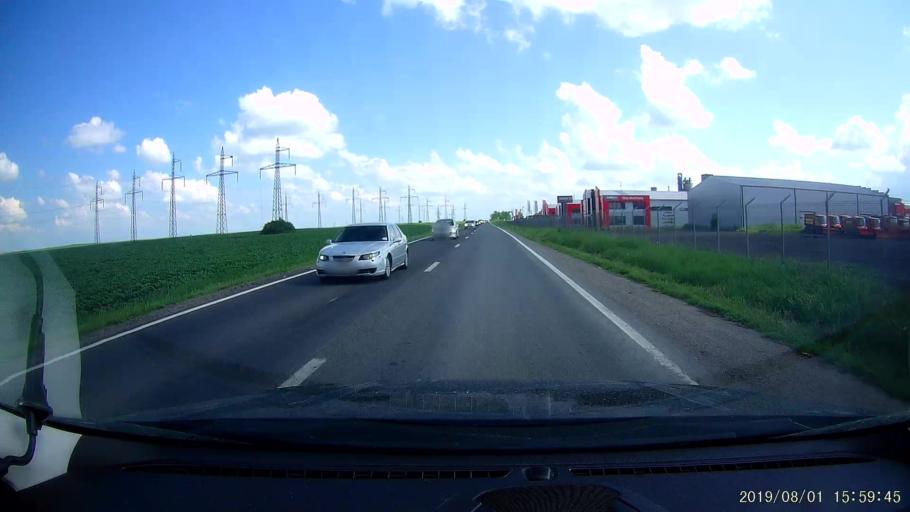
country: RO
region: Ialomita
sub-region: Comuna Slobozia
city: Slobozia
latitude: 44.5414
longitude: 27.3855
